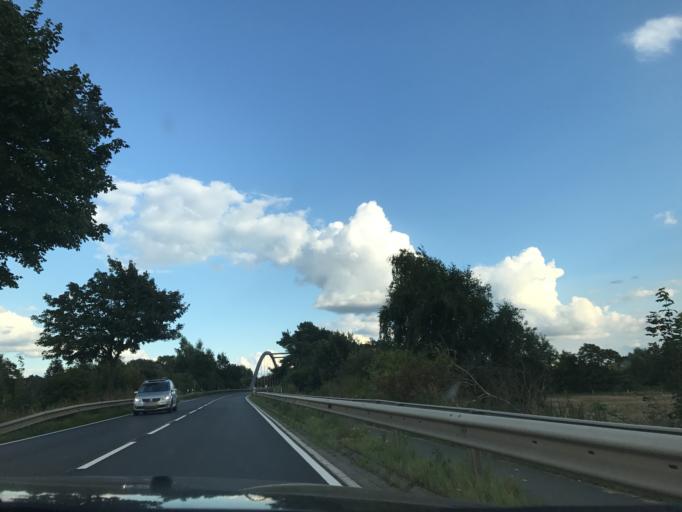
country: DE
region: Lower Saxony
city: Klein Schwulper
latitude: 52.3127
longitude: 10.4557
